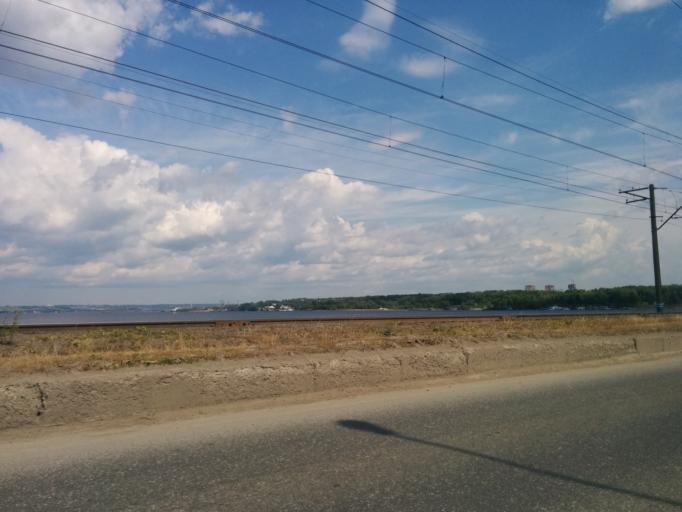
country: RU
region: Perm
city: Perm
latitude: 58.1150
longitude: 56.3507
